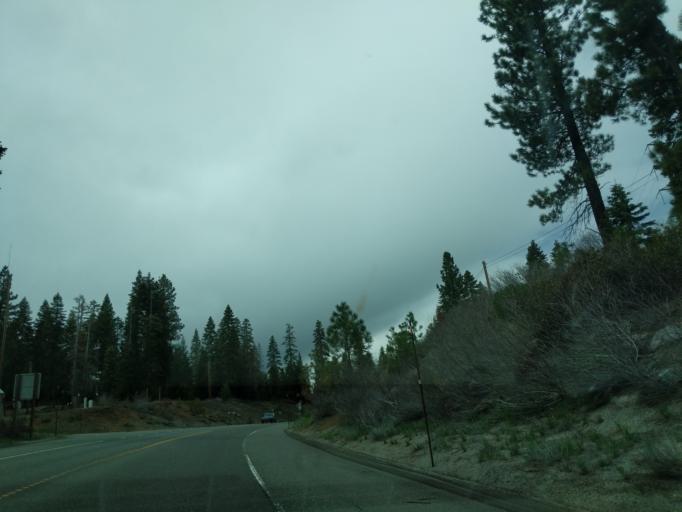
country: US
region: California
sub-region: Placer County
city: Tahoe Vista
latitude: 39.2602
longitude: -120.0710
